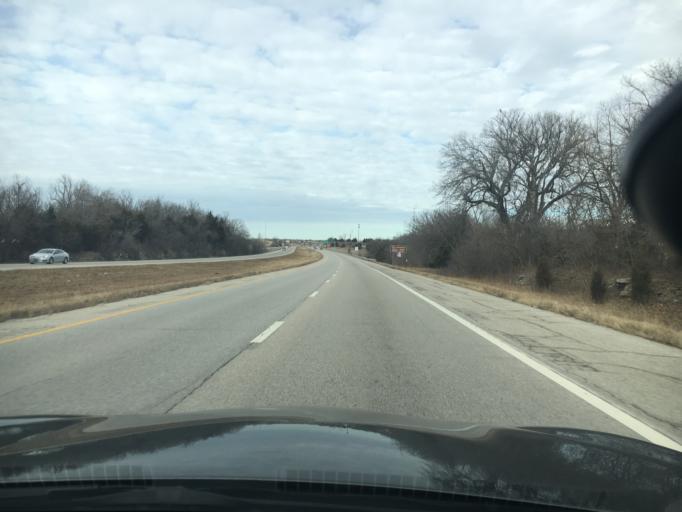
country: US
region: Missouri
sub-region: Cass County
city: Belton
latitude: 38.8211
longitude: -94.6760
